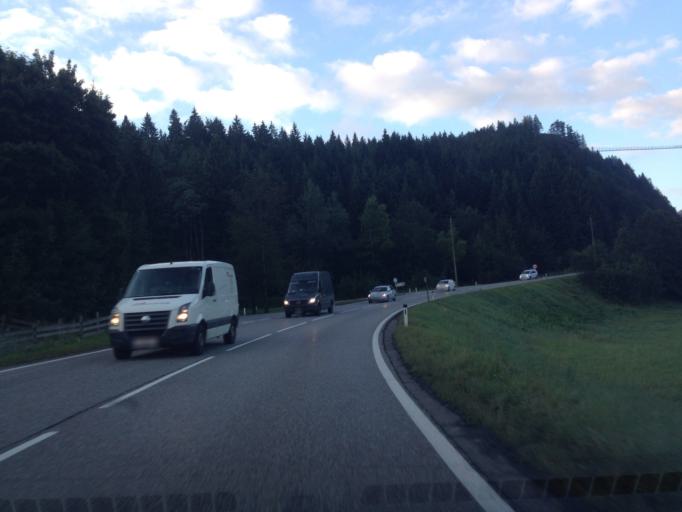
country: AT
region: Tyrol
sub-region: Politischer Bezirk Reutte
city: Breitenwang
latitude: 47.4687
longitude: 10.7255
